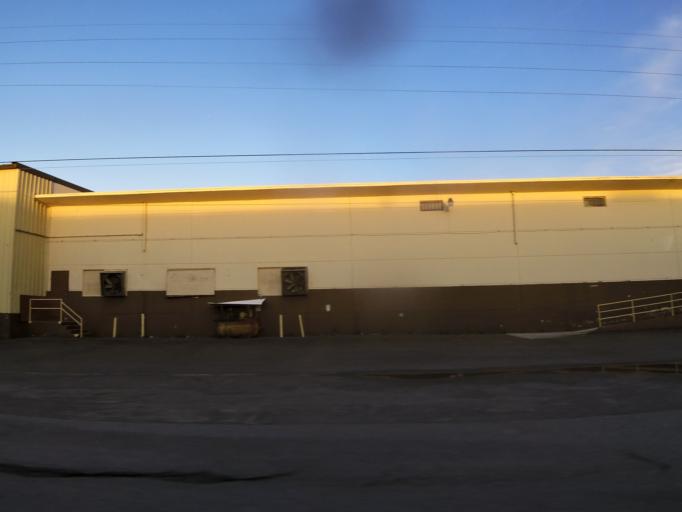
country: US
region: Florida
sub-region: Duval County
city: Jacksonville
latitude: 30.3469
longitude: -81.7111
